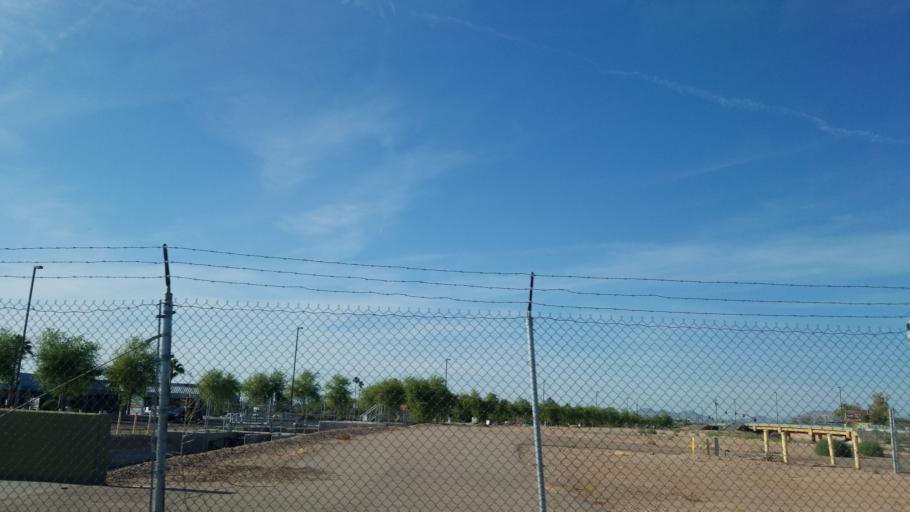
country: US
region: Arizona
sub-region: Maricopa County
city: Queen Creek
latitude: 33.3073
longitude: -111.6881
